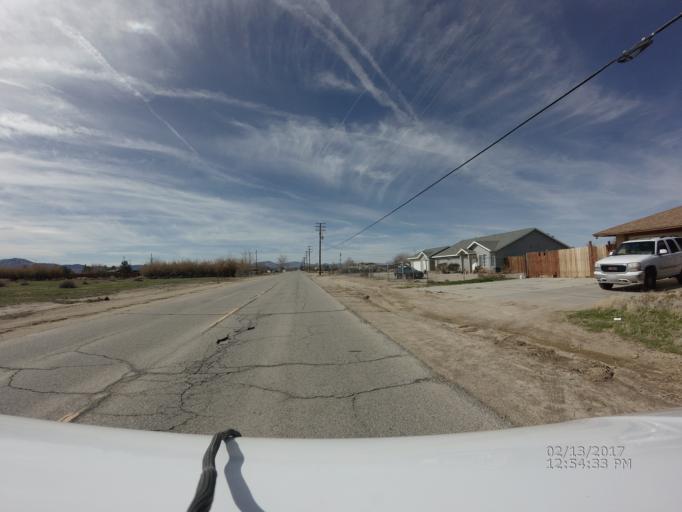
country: US
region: California
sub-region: Los Angeles County
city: Littlerock
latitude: 34.5725
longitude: -117.9548
